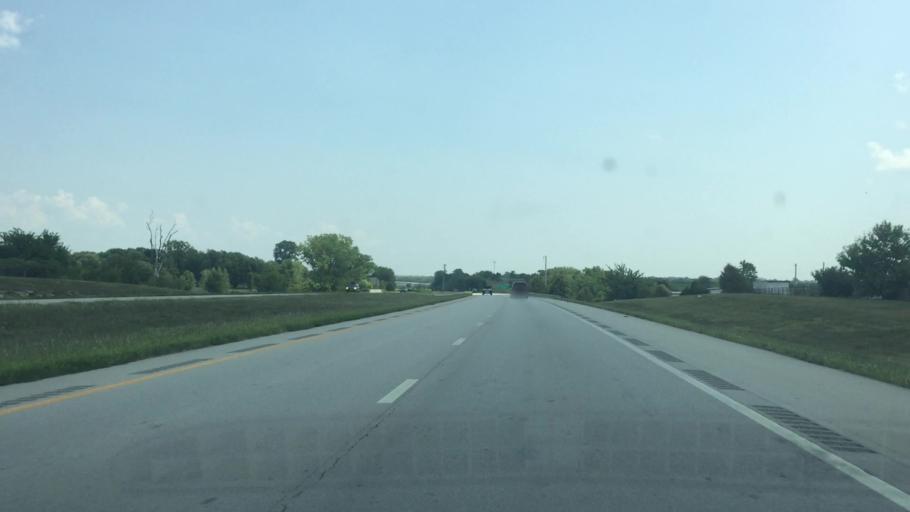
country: US
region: Kansas
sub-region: Johnson County
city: Edgerton
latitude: 38.7499
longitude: -94.9855
